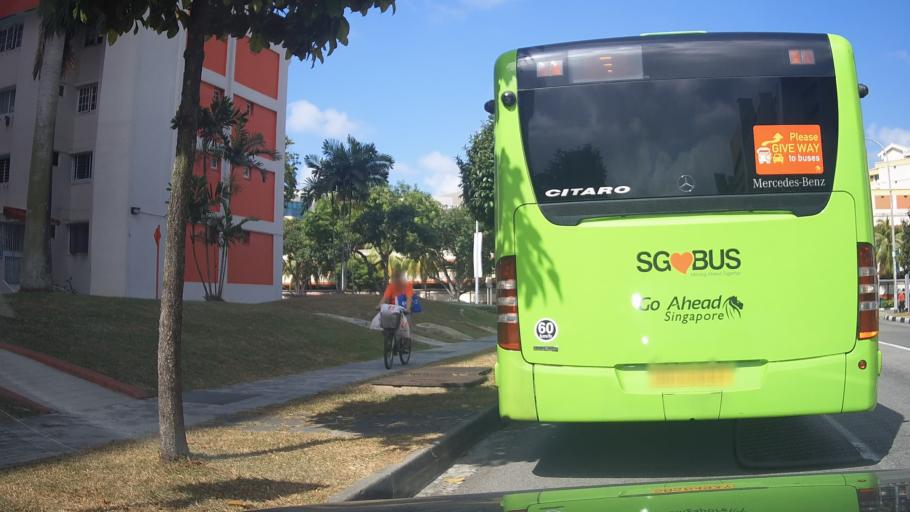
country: SG
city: Singapore
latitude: 1.3553
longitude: 103.9469
